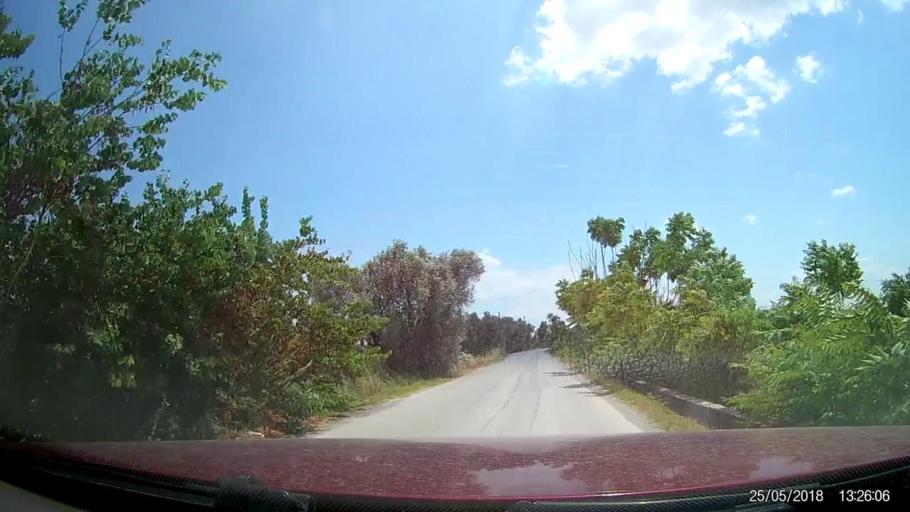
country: GR
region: Central Greece
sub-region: Nomos Evvoias
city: Mytikas
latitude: 38.4579
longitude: 23.6465
